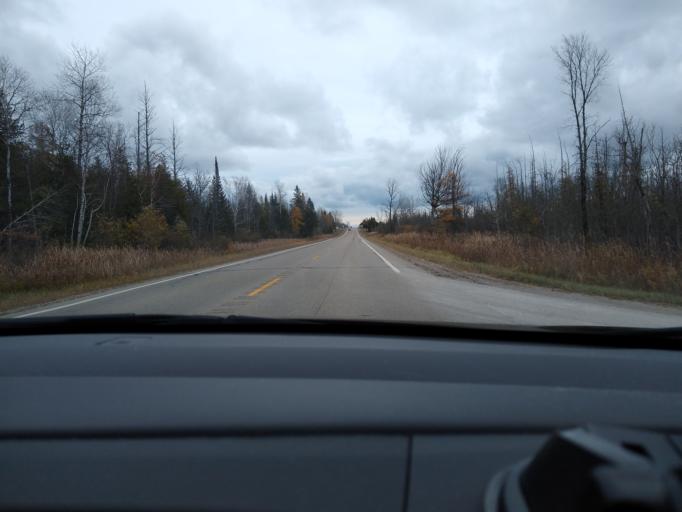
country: US
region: Michigan
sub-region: Delta County
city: Escanaba
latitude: 45.7834
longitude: -87.3307
